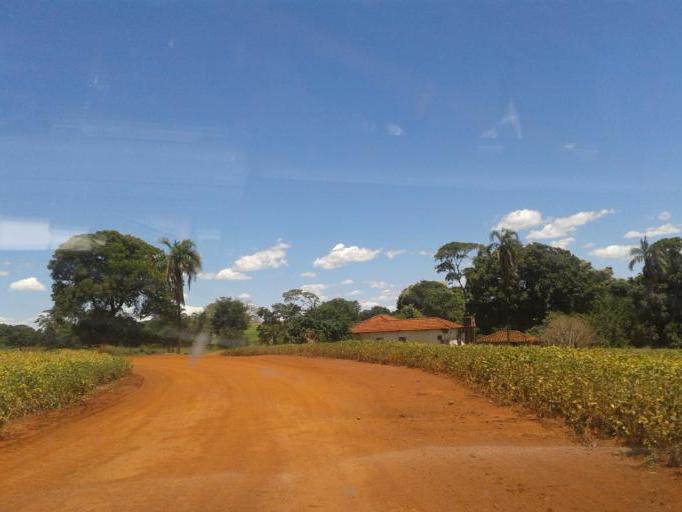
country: BR
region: Minas Gerais
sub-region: Capinopolis
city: Capinopolis
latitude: -18.5962
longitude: -49.5311
